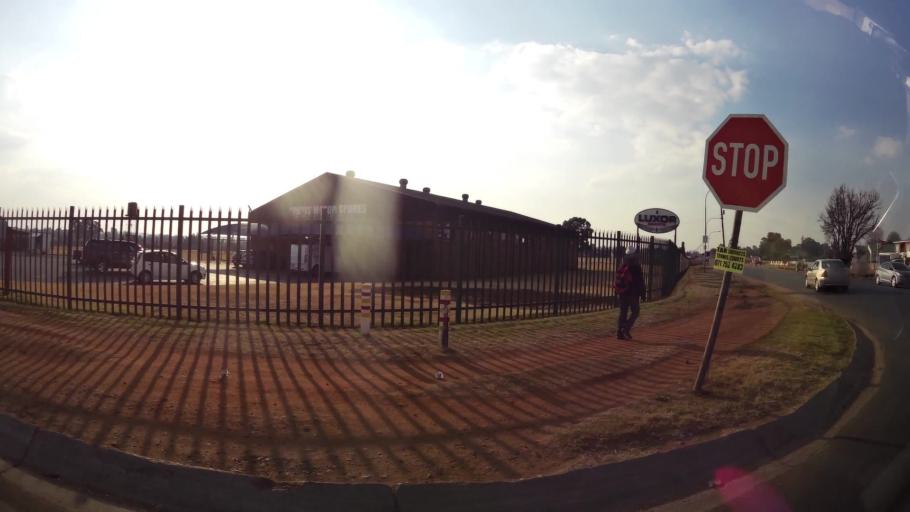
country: ZA
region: Gauteng
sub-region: Ekurhuleni Metropolitan Municipality
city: Benoni
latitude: -26.1097
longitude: 28.2955
